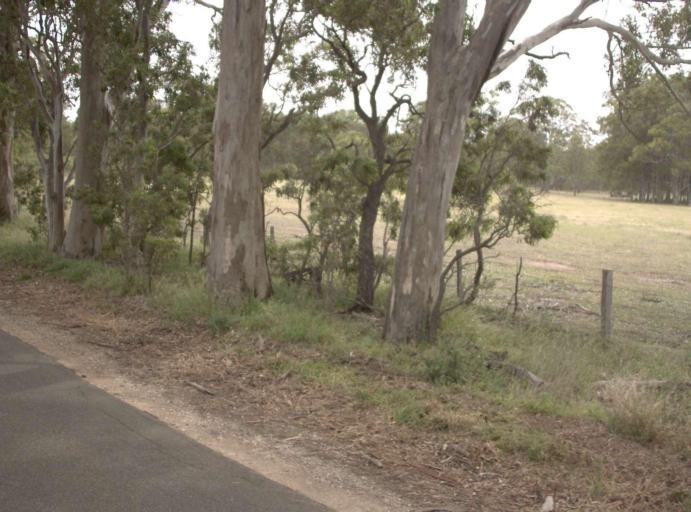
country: AU
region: Victoria
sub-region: Wellington
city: Sale
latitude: -37.8659
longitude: 147.0682
